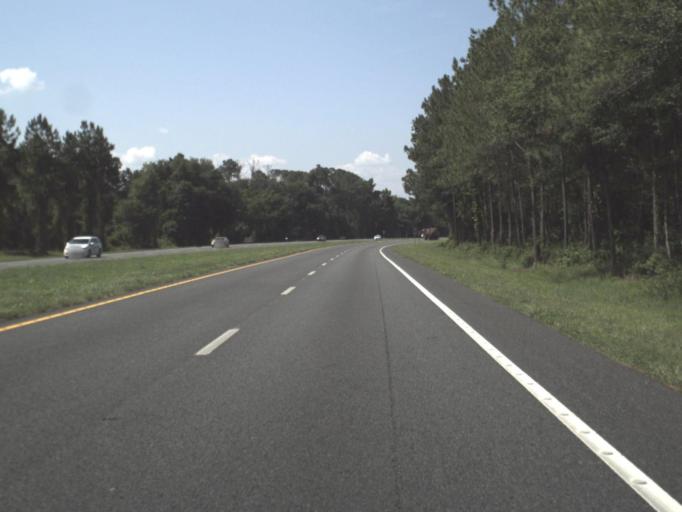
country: US
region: Florida
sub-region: Marion County
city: Citra
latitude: 29.4724
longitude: -82.1047
